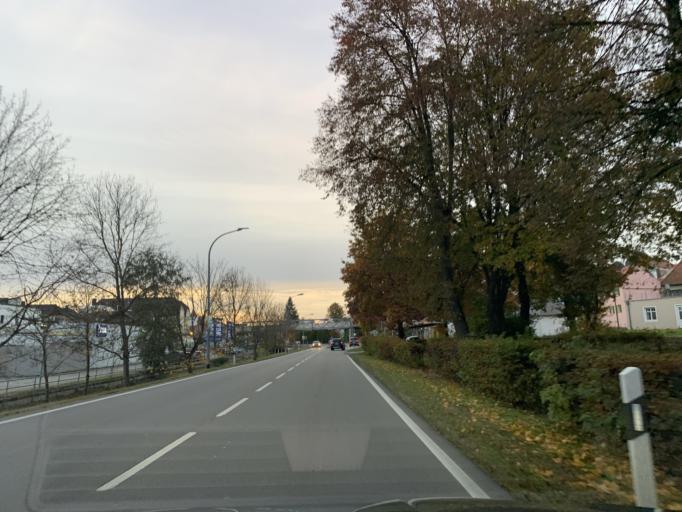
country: DE
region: Bavaria
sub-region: Upper Palatinate
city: Neunburg vorm Wald
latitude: 49.3467
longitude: 12.3855
